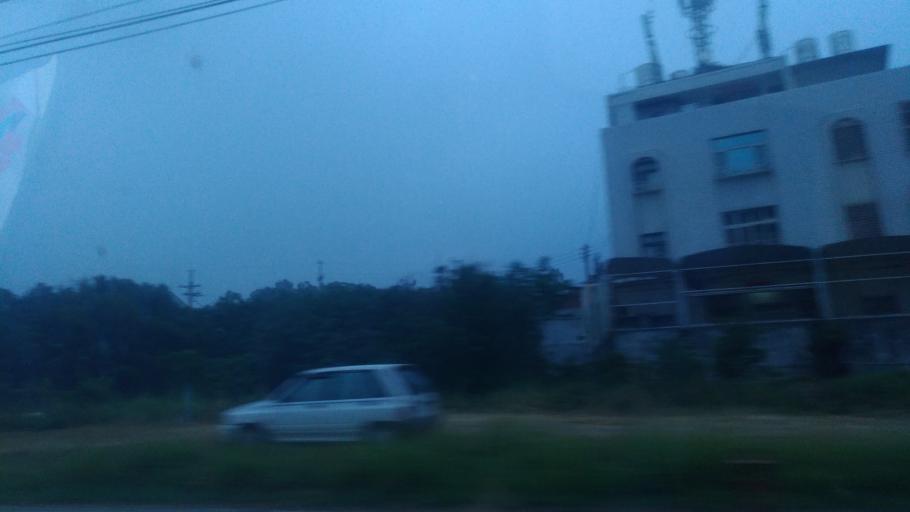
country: TW
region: Taiwan
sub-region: Miaoli
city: Miaoli
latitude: 24.5648
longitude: 120.7105
